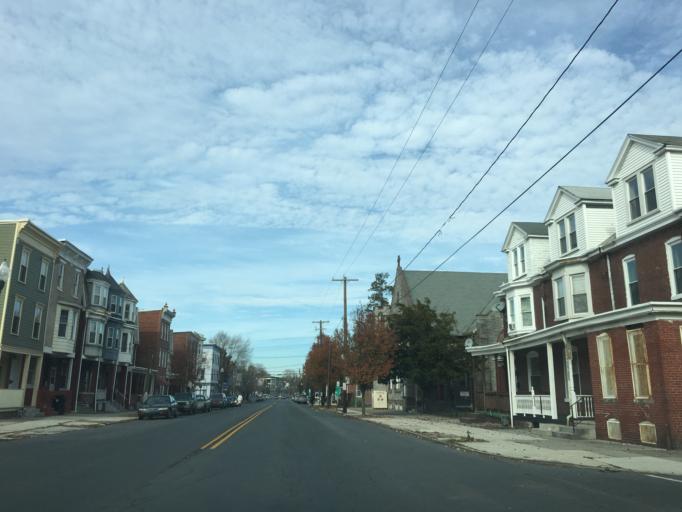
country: US
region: Pennsylvania
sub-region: Dauphin County
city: Harrisburg
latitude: 40.2844
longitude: -76.8924
